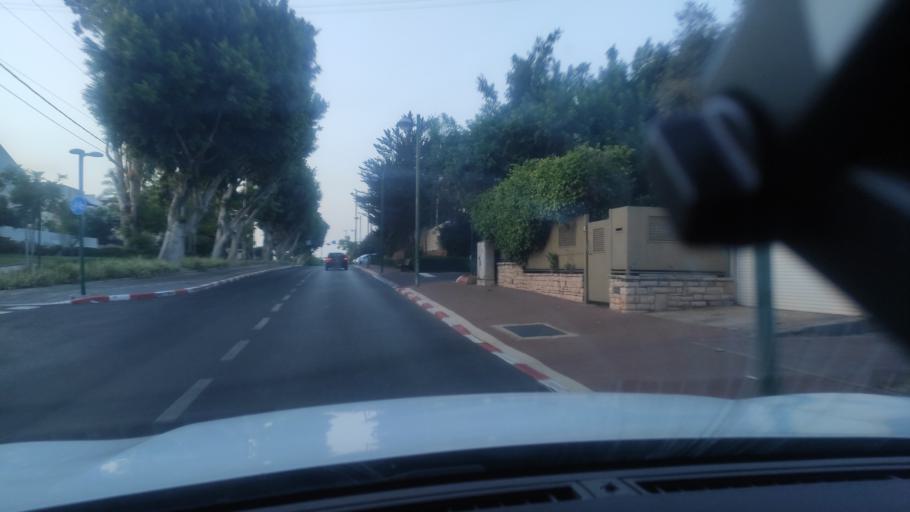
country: IL
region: Central District
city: Kfar Saba
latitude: 32.1825
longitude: 34.9044
